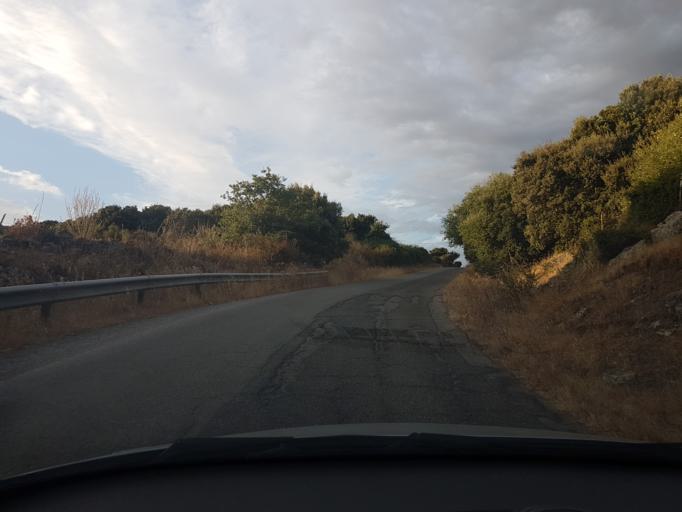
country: IT
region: Sardinia
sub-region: Provincia di Oristano
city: Seneghe
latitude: 40.1010
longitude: 8.6210
